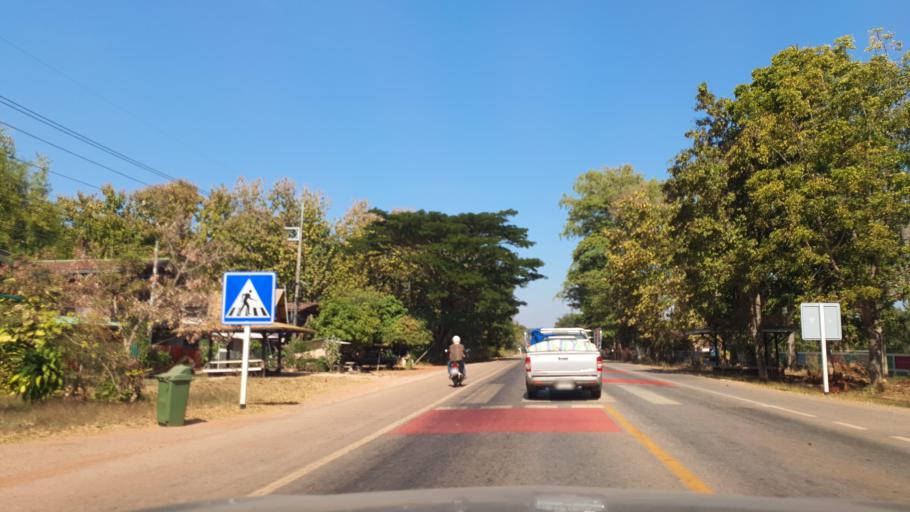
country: TH
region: Sakon Nakhon
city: Phu Phan
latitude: 17.0821
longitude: 103.9811
